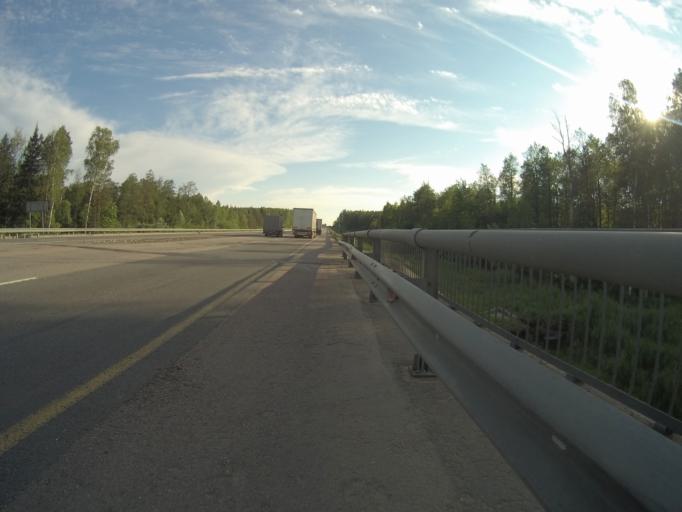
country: RU
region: Vladimir
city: Sudogda
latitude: 56.1239
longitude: 40.8630
